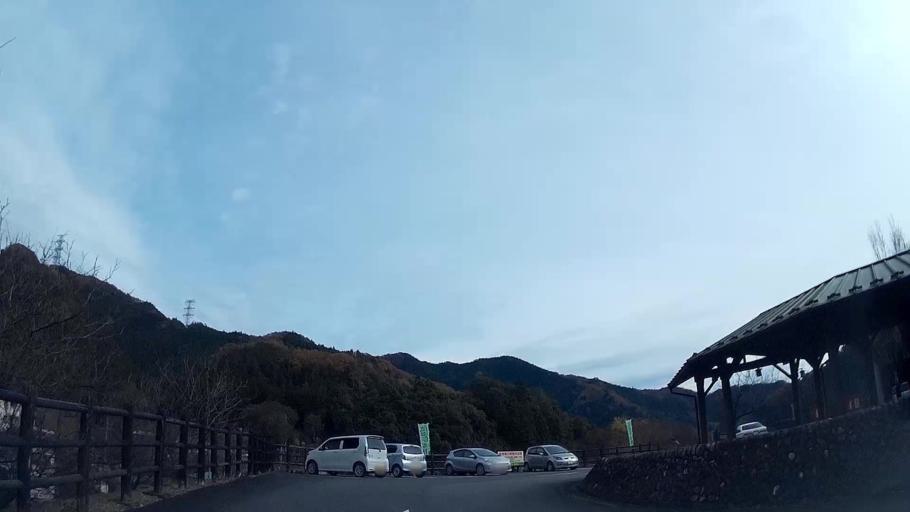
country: JP
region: Saitama
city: Chichibu
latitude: 36.0600
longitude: 138.9674
